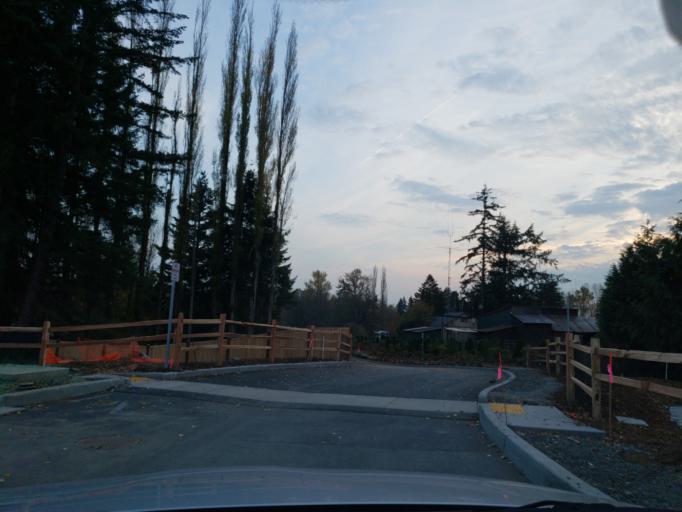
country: US
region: Washington
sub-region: King County
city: Bothell
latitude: 47.7815
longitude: -122.2247
